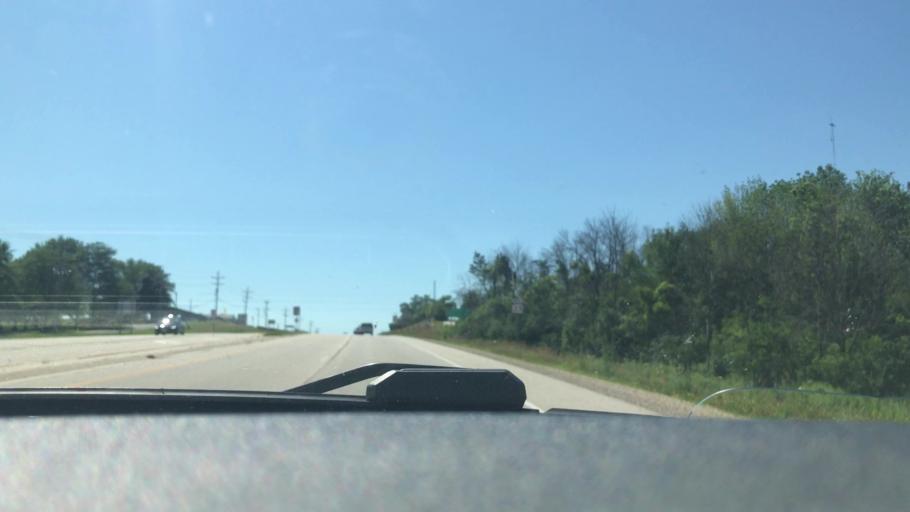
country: US
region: Wisconsin
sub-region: Washington County
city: West Bend
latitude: 43.4277
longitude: -88.2625
